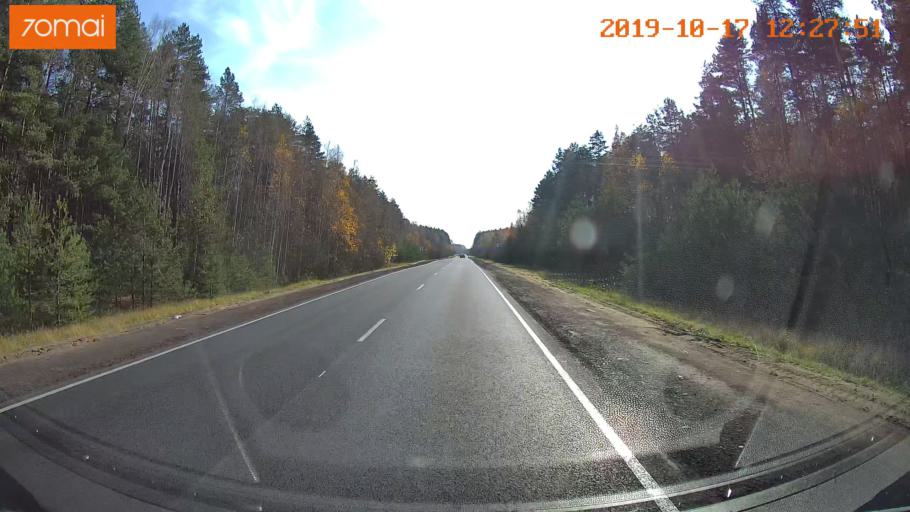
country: RU
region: Rjazan
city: Syntul
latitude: 54.9976
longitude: 41.2655
